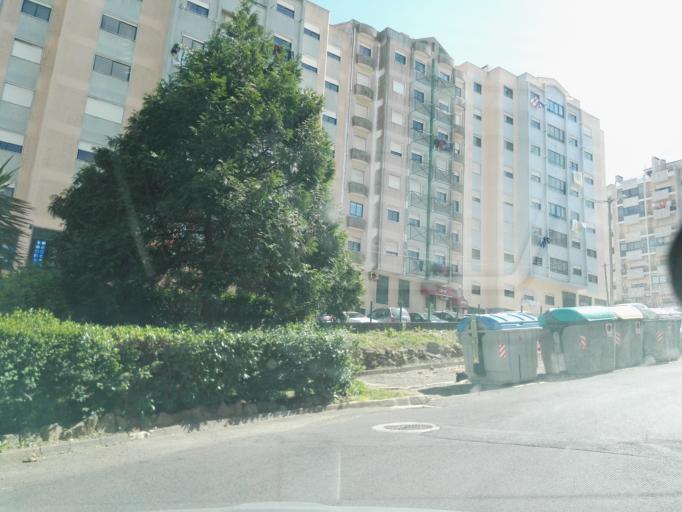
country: PT
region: Lisbon
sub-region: Sintra
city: Sintra
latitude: 38.7969
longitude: -9.3535
